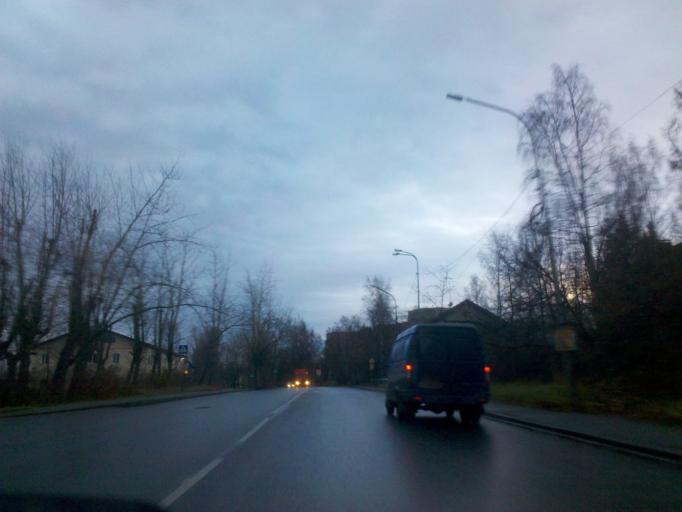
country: RU
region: Republic of Karelia
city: Petrozavodsk
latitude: 61.7823
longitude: 34.4002
